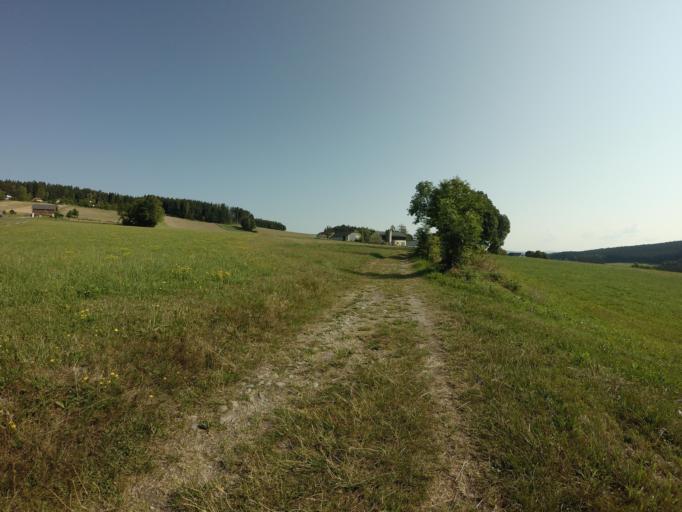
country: AT
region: Upper Austria
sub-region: Politischer Bezirk Urfahr-Umgebung
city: Bad Leonfelden
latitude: 48.5452
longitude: 14.3203
